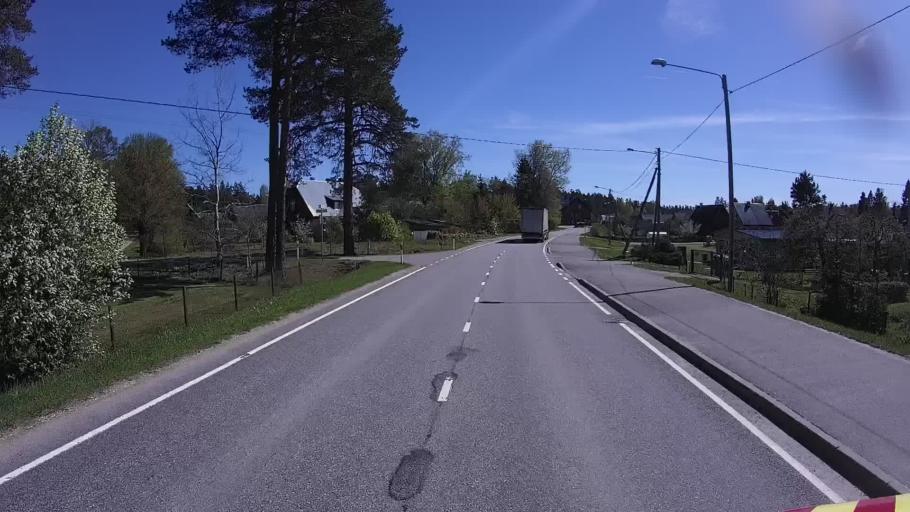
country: EE
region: Harju
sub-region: Kuusalu vald
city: Kuusalu
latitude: 59.2840
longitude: 25.6129
